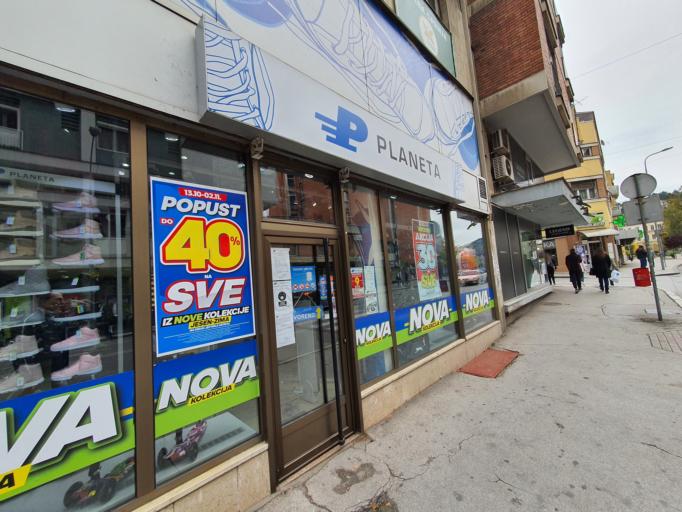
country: RS
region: Central Serbia
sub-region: Zlatiborski Okrug
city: Uzice
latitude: 43.8561
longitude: 19.8409
